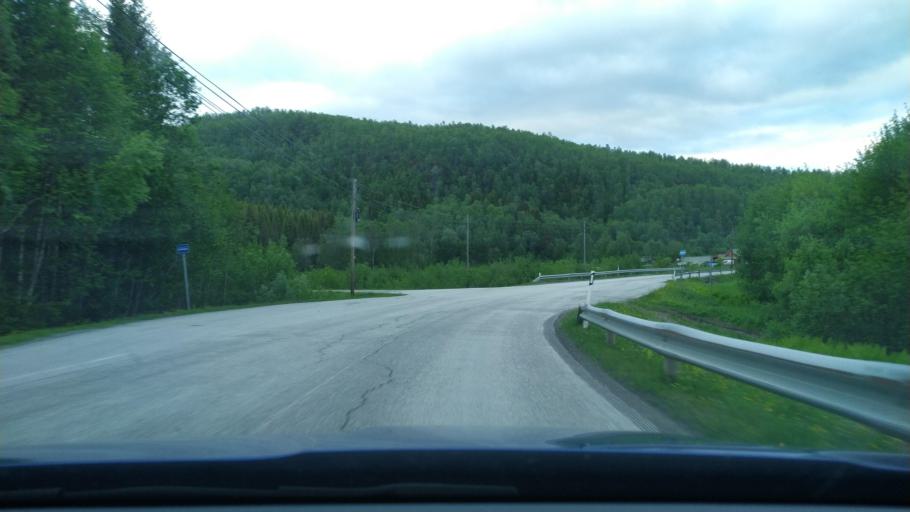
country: NO
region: Troms
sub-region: Dyroy
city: Brostadbotn
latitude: 69.0716
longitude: 17.7311
